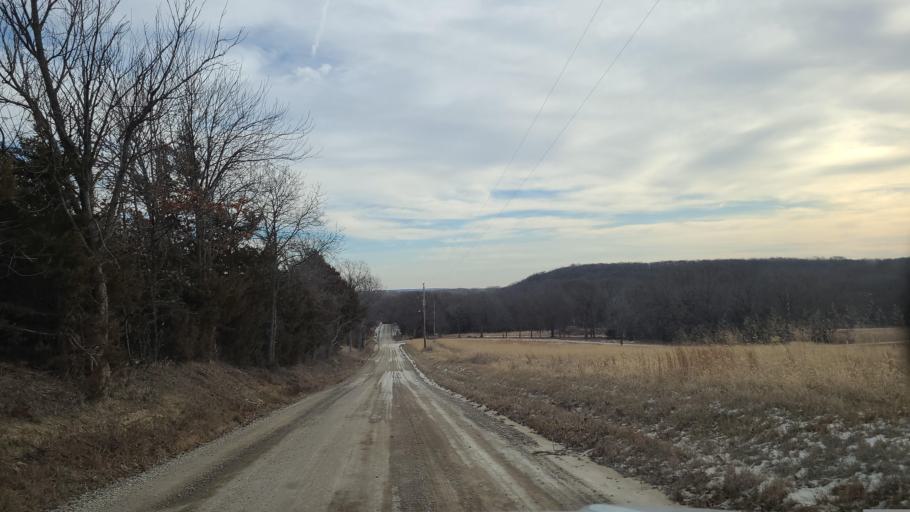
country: US
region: Kansas
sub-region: Douglas County
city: Lawrence
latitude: 39.0368
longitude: -95.3773
